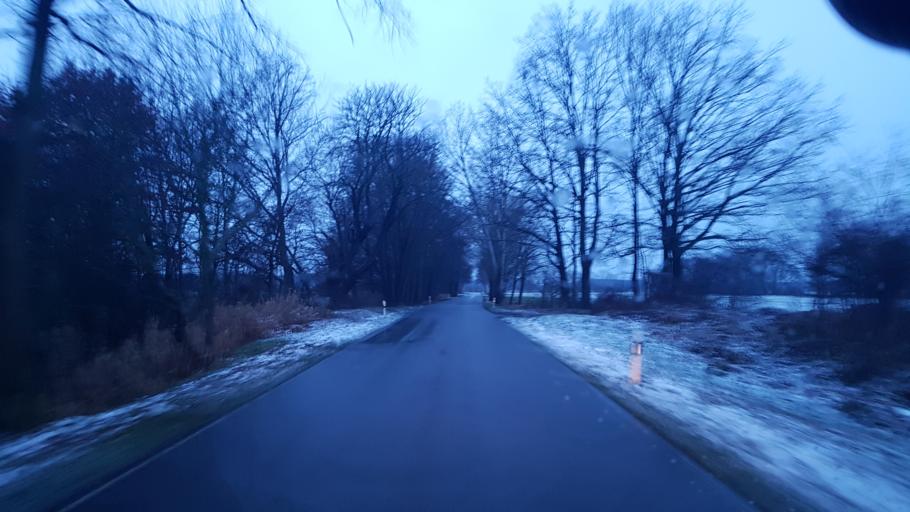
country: DE
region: Brandenburg
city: Peitz
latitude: 51.8260
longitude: 14.3828
